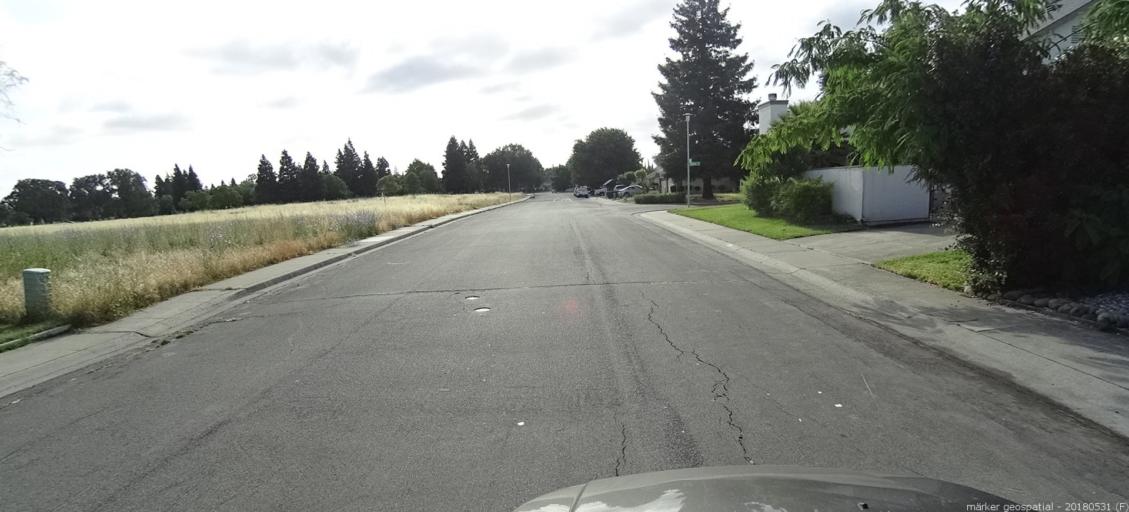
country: US
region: California
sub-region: Sacramento County
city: Sacramento
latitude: 38.6290
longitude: -121.4906
